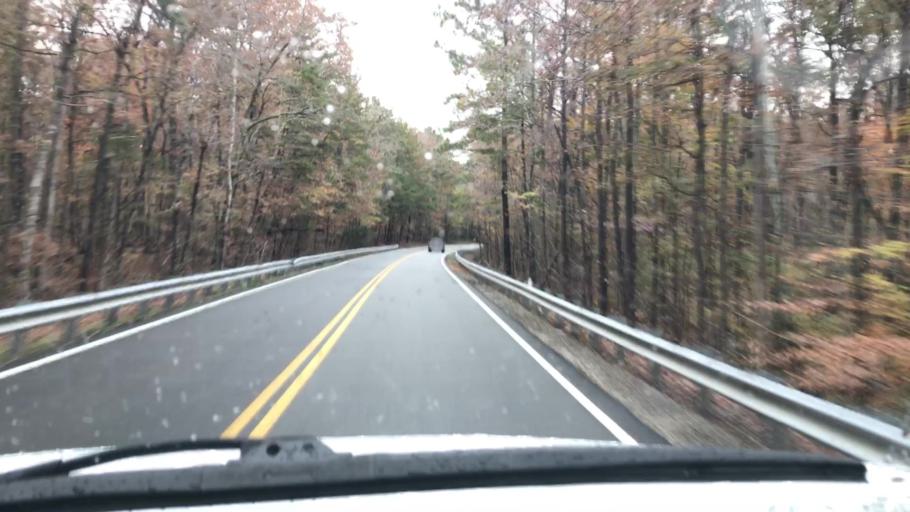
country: US
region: Virginia
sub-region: Henrico County
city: Short Pump
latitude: 37.6054
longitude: -77.6984
